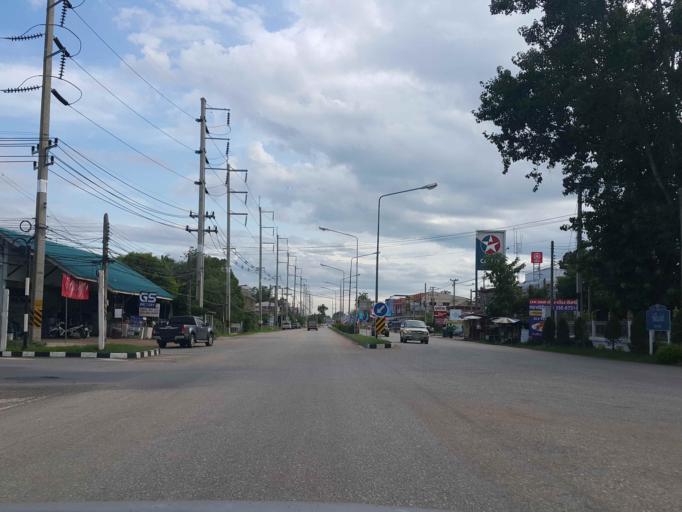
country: TH
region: Sukhothai
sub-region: Amphoe Si Satchanalai
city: Si Satchanalai
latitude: 17.5301
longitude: 99.7689
